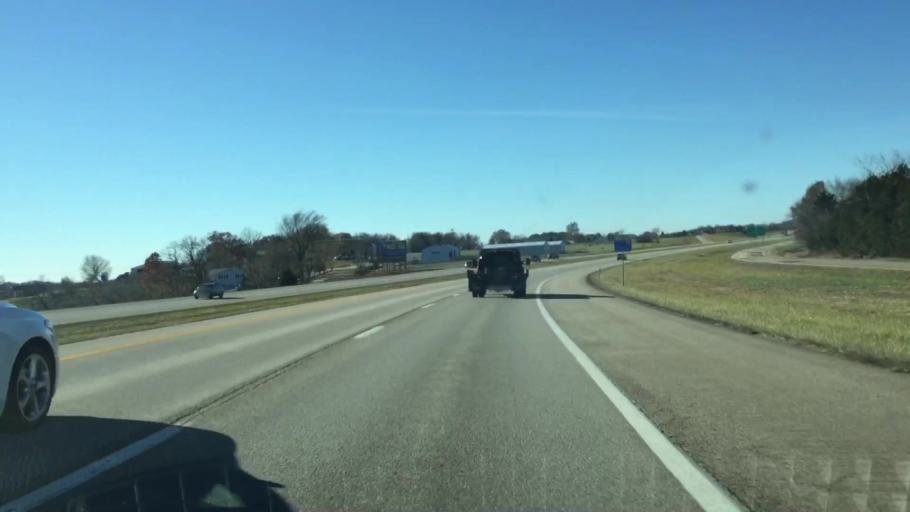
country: US
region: Missouri
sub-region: Miller County
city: Tuscumbia
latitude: 38.3838
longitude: -92.3903
